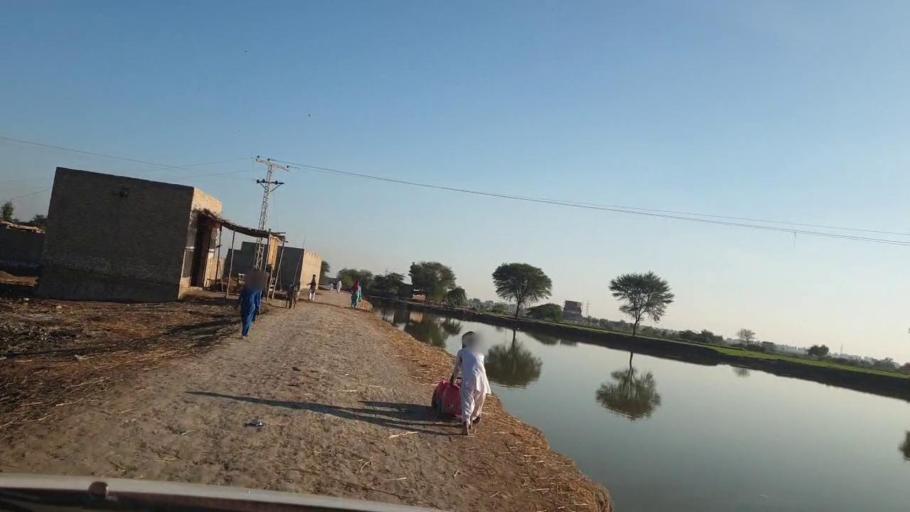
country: PK
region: Sindh
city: Khairpur Nathan Shah
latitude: 27.0459
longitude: 67.7254
